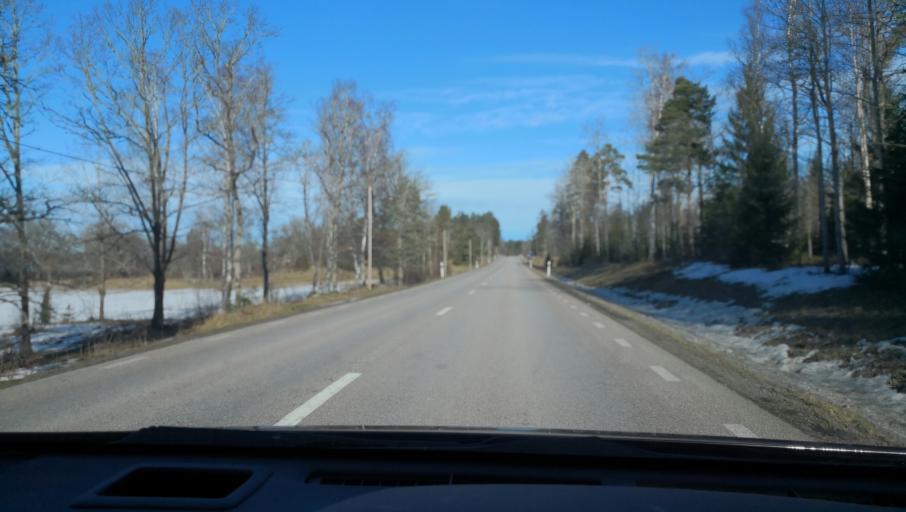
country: SE
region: Uppsala
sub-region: Osthammars Kommun
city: Osterbybruk
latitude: 60.1633
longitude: 17.8412
